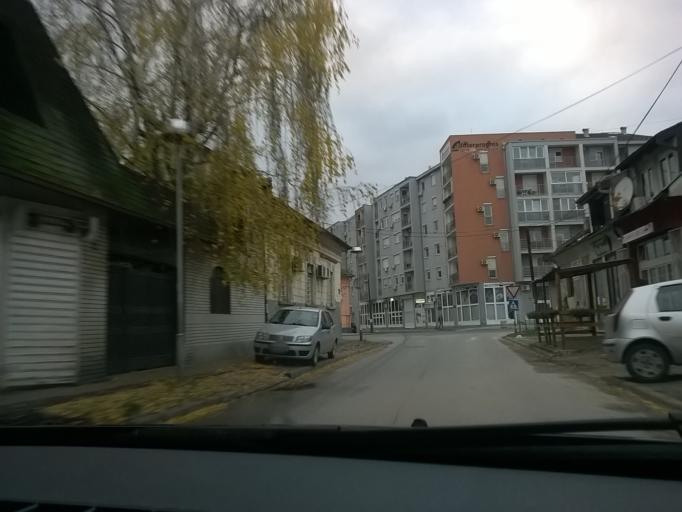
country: RS
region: Autonomna Pokrajina Vojvodina
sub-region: Juznobacki Okrug
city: Novi Sad
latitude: 45.2632
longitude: 19.8445
